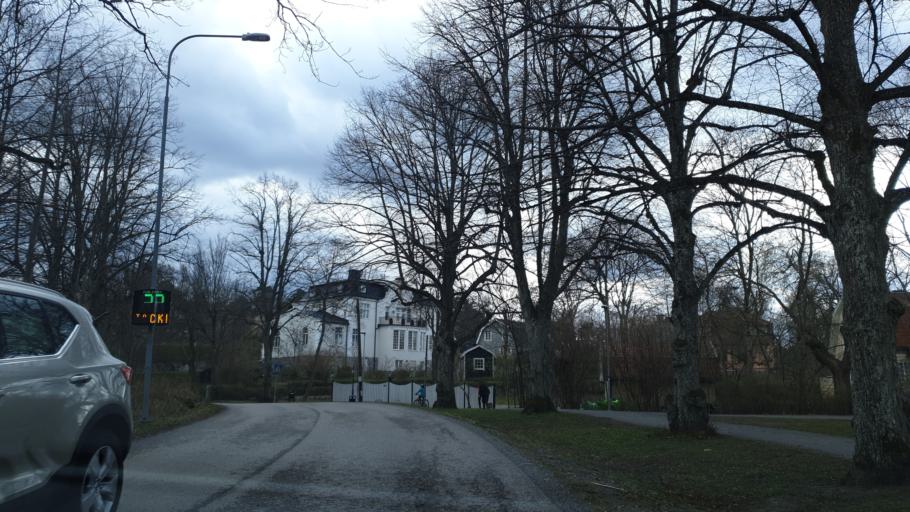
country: SE
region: Stockholm
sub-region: Nacka Kommun
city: Saltsjobaden
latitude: 59.2817
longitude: 18.3018
